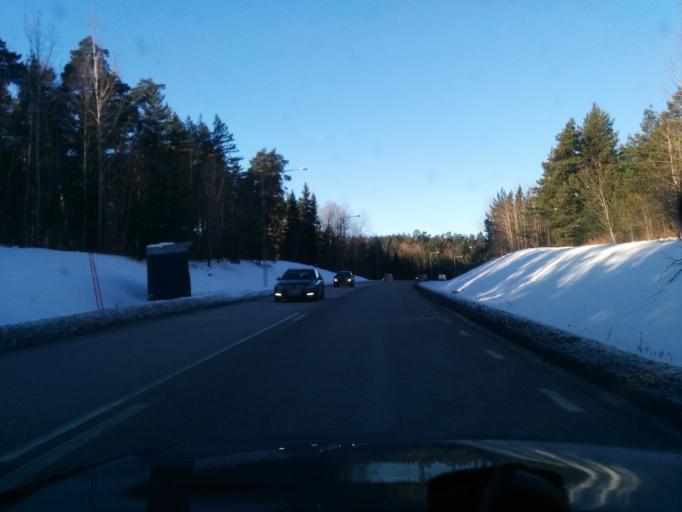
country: SE
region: Stockholm
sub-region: Taby Kommun
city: Taby
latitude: 59.4653
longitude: 18.1184
